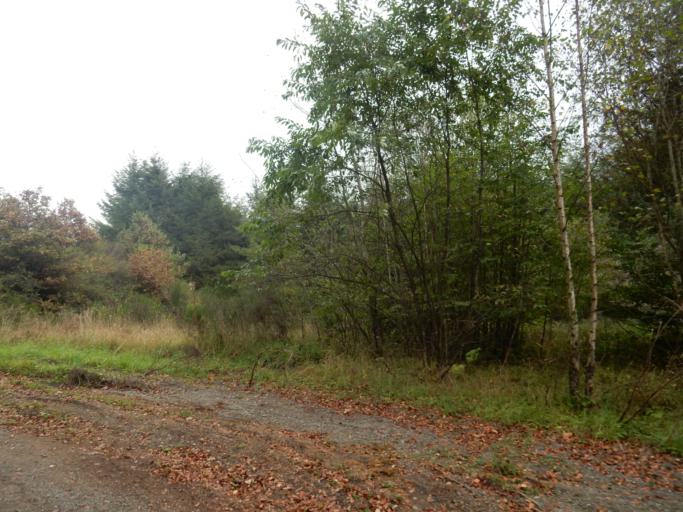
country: LU
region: Diekirch
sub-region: Canton de Wiltz
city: Winseler
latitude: 49.9562
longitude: 5.8937
